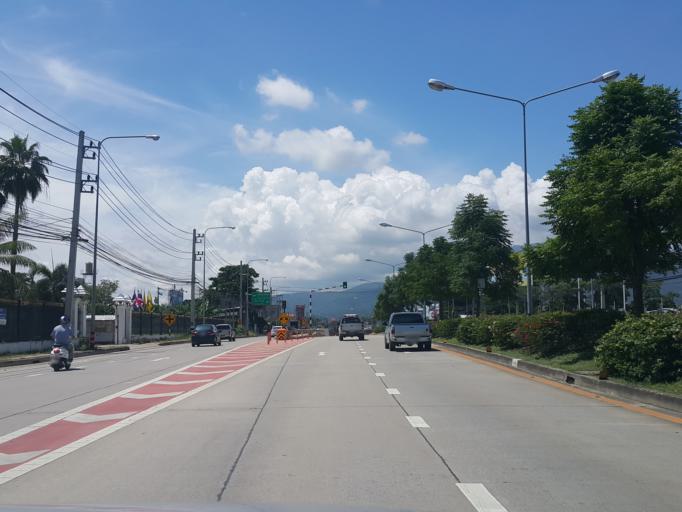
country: TH
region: Chiang Mai
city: Chiang Mai
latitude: 18.7415
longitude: 98.9619
